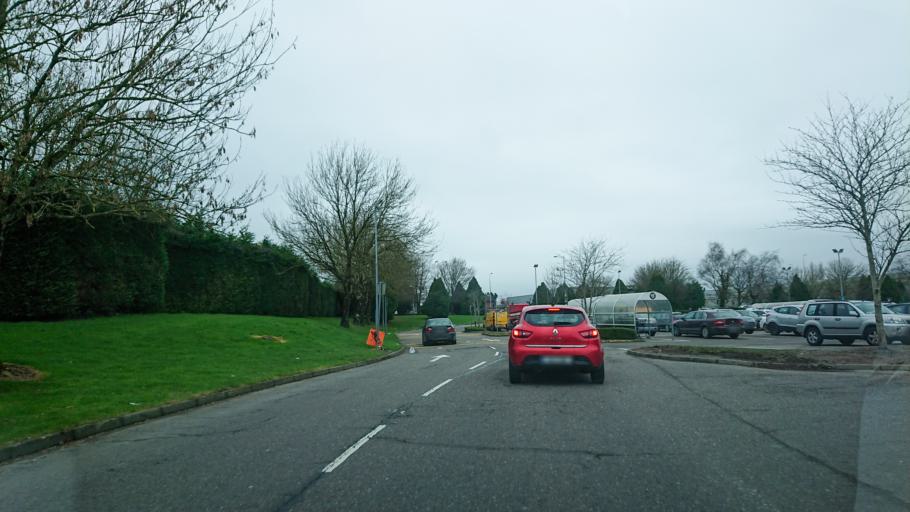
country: IE
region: Munster
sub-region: County Cork
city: Cork
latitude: 51.8730
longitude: -8.5211
